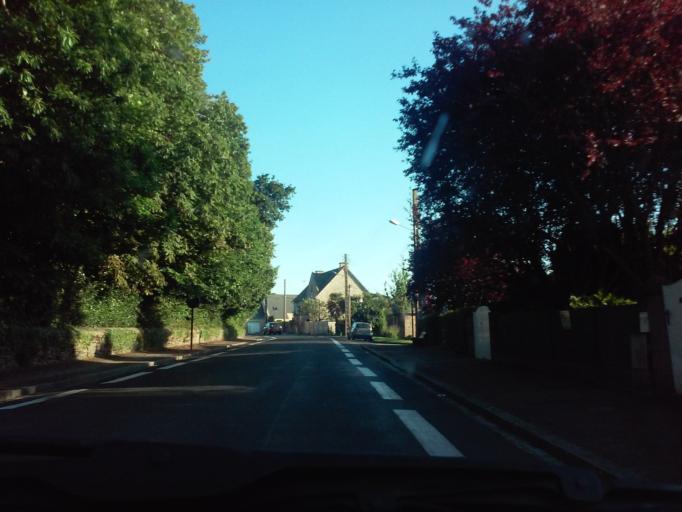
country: FR
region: Brittany
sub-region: Departement d'Ille-et-Vilaine
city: Dinard
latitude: 48.6253
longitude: -2.0593
